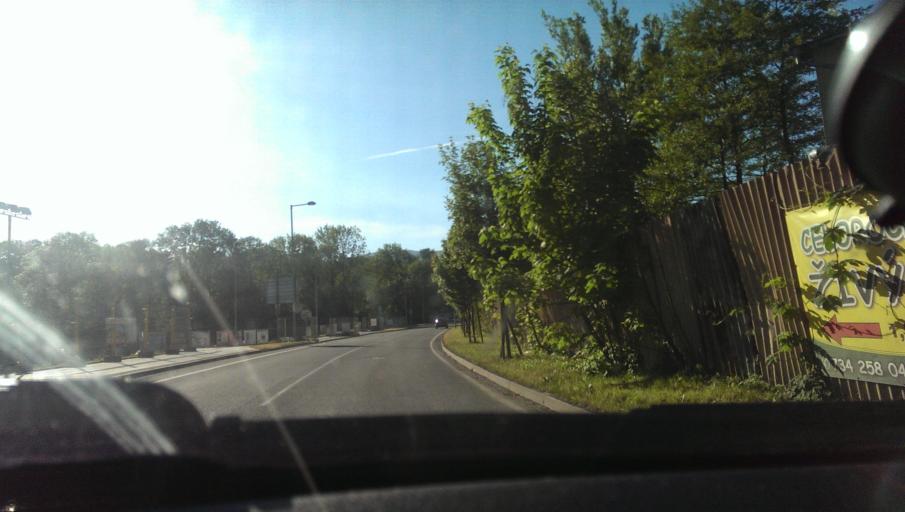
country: CZ
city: Frydlant nad Ostravici
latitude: 49.5850
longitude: 18.3626
